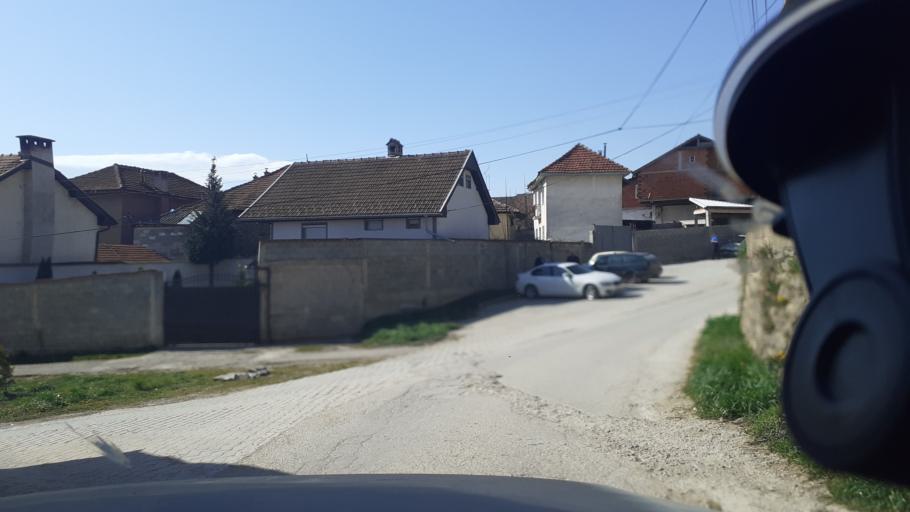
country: MK
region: Tearce
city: Slatino
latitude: 42.0680
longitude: 21.0388
